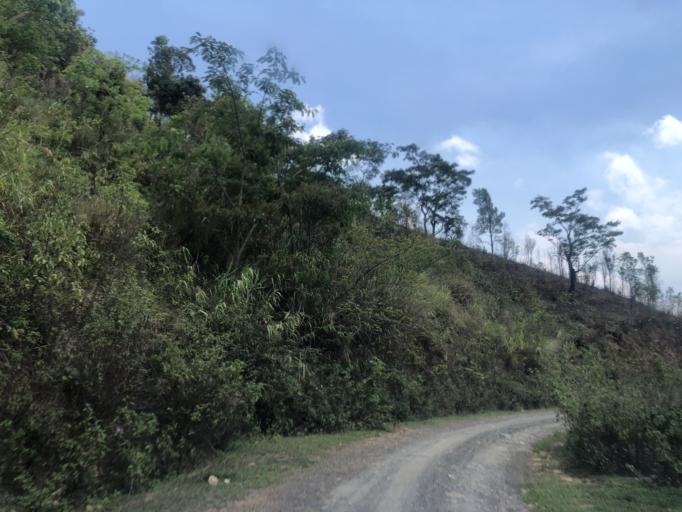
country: LA
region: Phongsali
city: Phongsali
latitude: 21.4359
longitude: 102.1612
